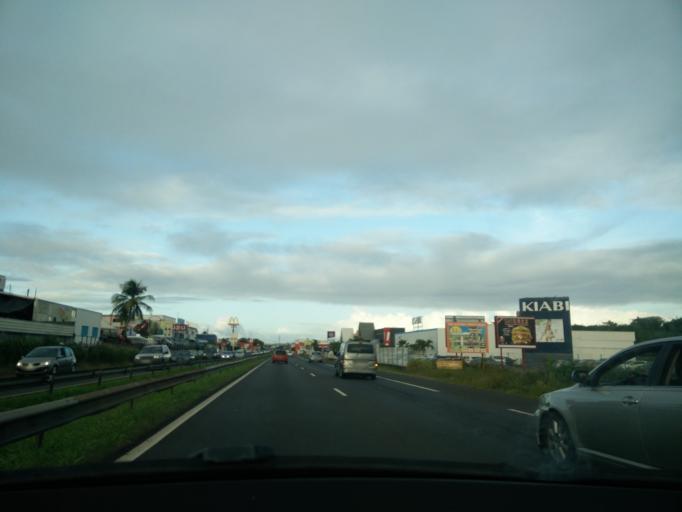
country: GP
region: Guadeloupe
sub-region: Guadeloupe
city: Baie-Mahault
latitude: 16.2542
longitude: -61.5668
